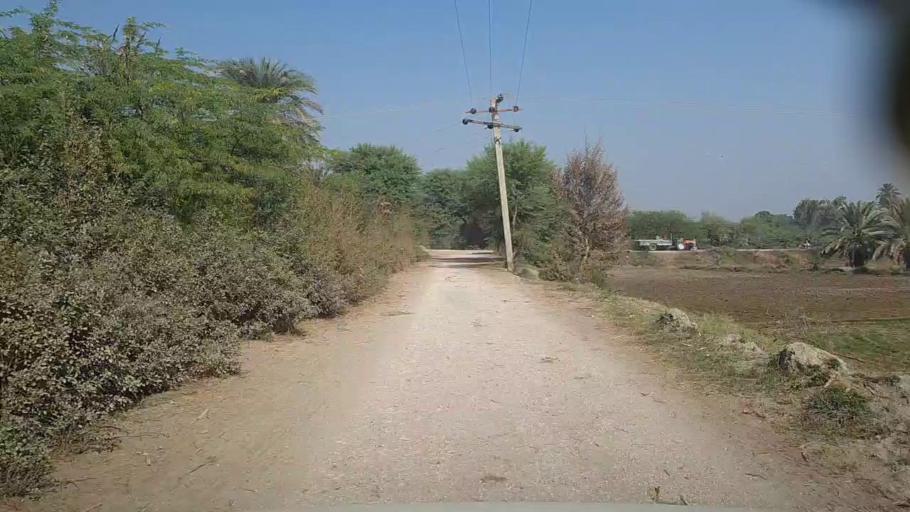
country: PK
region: Sindh
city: Karaundi
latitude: 26.9603
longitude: 68.4201
